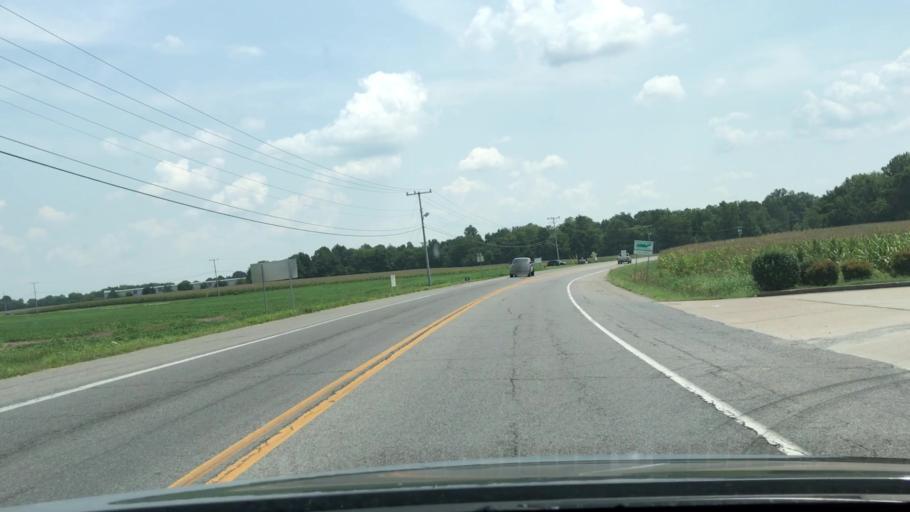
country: US
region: Tennessee
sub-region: Sumner County
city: Portland
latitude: 36.5900
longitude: -86.5918
